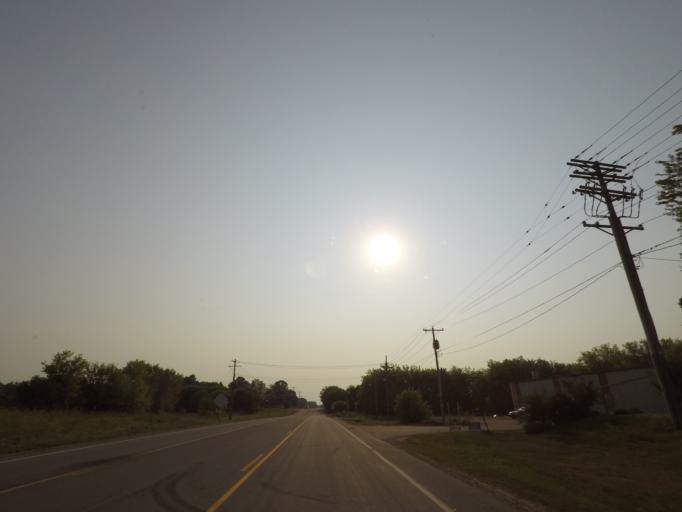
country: US
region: Wisconsin
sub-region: Dane County
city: McFarland
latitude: 43.0520
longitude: -89.2745
